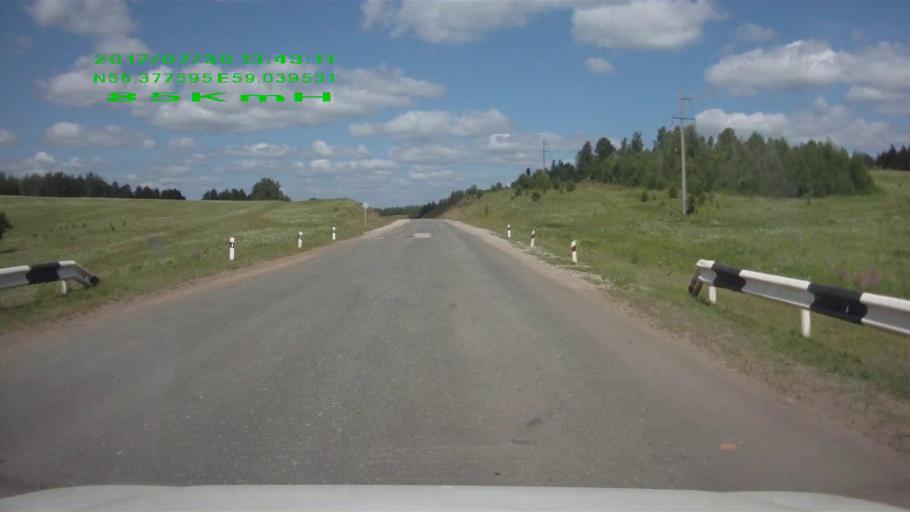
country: RU
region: Sverdlovsk
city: Mikhaylovsk
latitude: 56.3779
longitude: 59.0395
